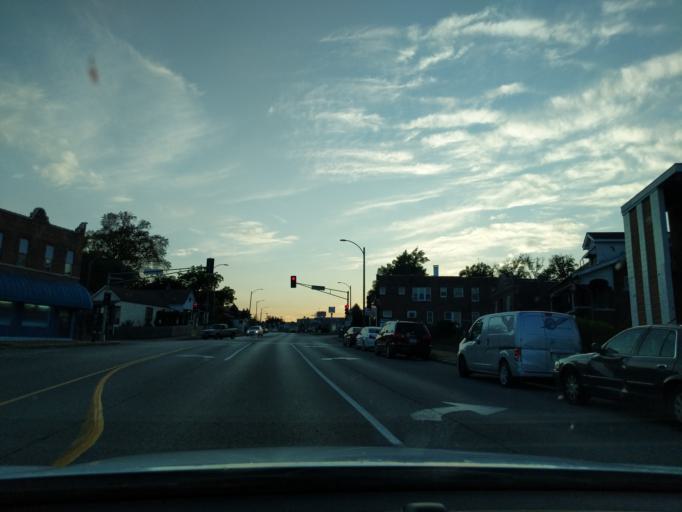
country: US
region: Missouri
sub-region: Saint Louis County
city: Richmond Heights
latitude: 38.6111
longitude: -90.2744
